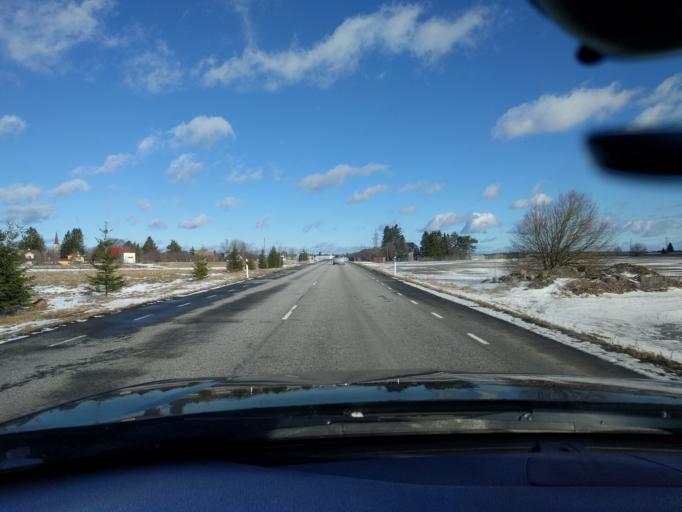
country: EE
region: Harju
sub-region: Raasiku vald
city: Raasiku
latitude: 59.3677
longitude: 25.1908
